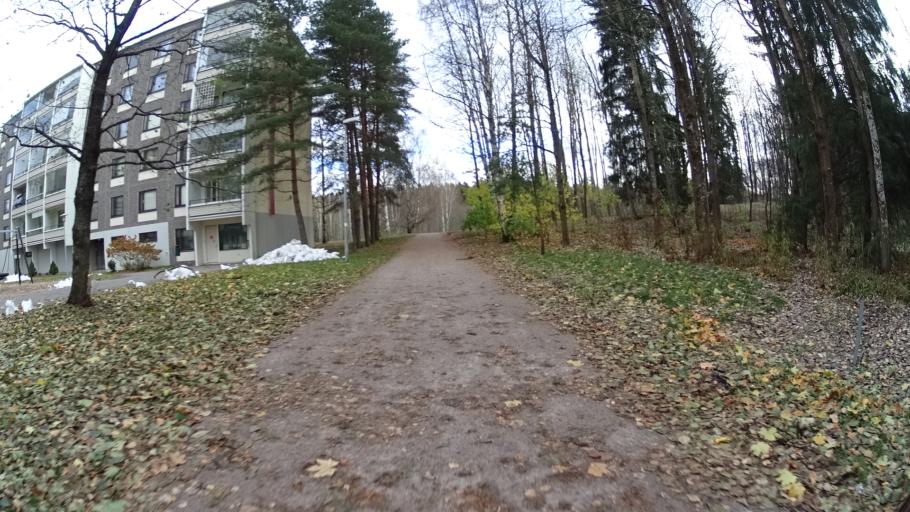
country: FI
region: Uusimaa
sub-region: Helsinki
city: Teekkarikylae
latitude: 60.2628
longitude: 24.8590
